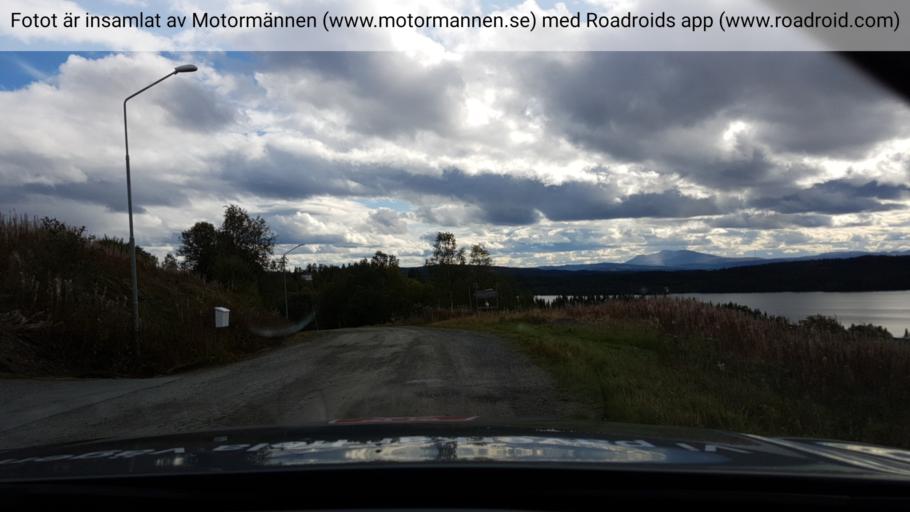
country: SE
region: Jaemtland
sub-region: Are Kommun
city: Are
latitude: 63.7509
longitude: 12.9586
